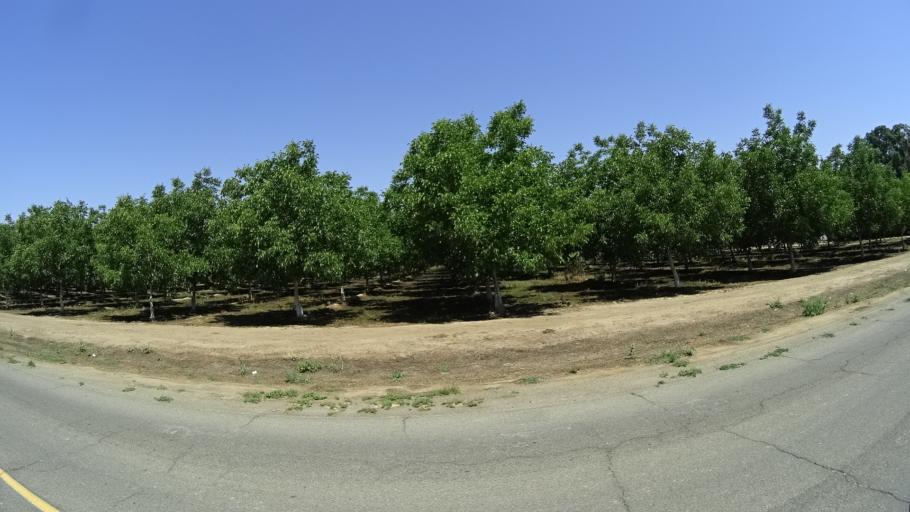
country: US
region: California
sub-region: Kings County
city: Lucerne
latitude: 36.3571
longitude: -119.6840
